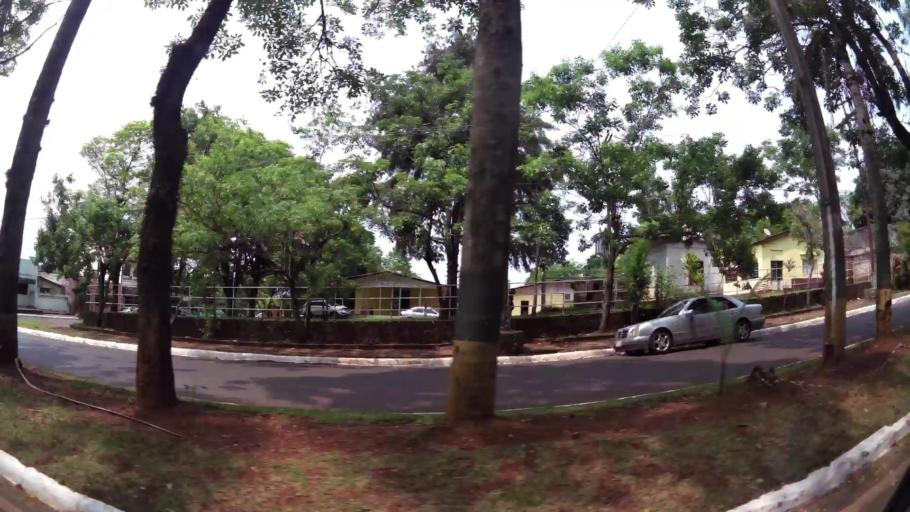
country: BR
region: Parana
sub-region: Foz Do Iguacu
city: Foz do Iguacu
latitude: -25.5576
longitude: -54.6018
